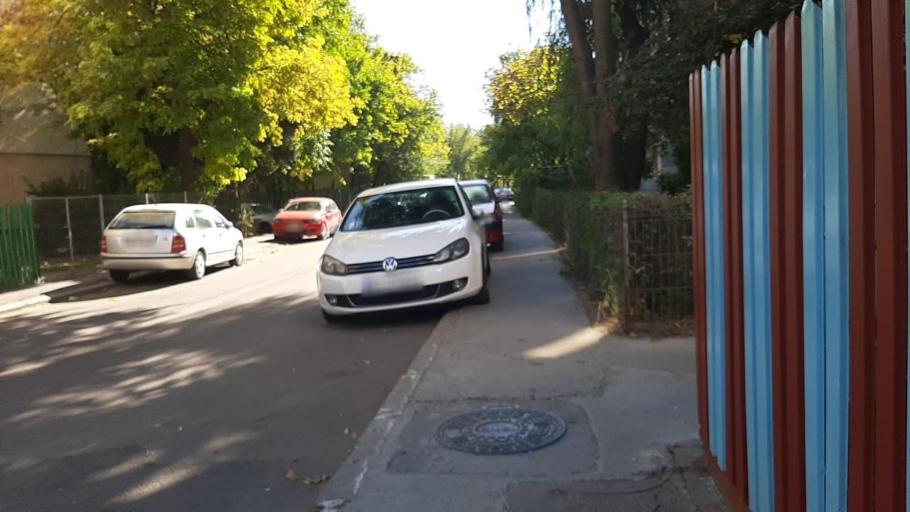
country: RO
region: Galati
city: Galati
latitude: 45.4425
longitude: 28.0248
